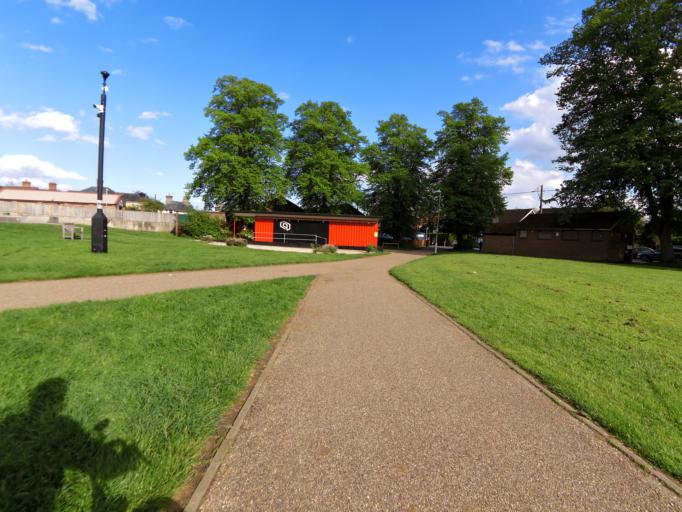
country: GB
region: England
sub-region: Suffolk
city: Stowmarket
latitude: 52.1888
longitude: 0.9894
